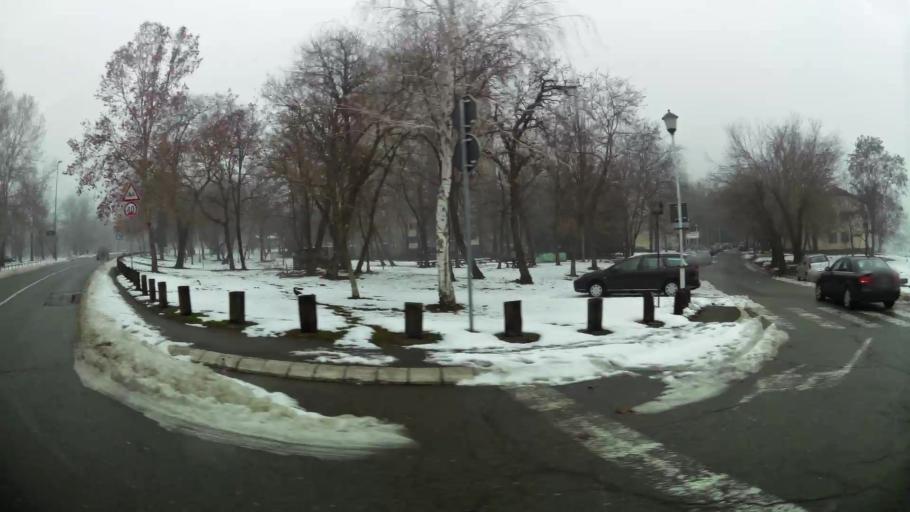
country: RS
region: Central Serbia
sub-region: Belgrade
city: Savski Venac
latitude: 44.7911
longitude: 20.4571
